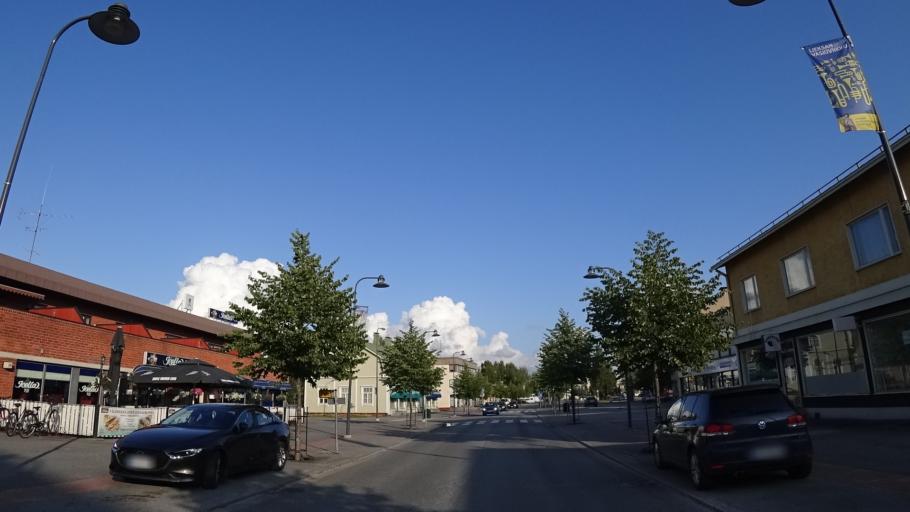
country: FI
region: North Karelia
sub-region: Pielisen Karjala
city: Lieksa
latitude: 63.3180
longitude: 30.0281
